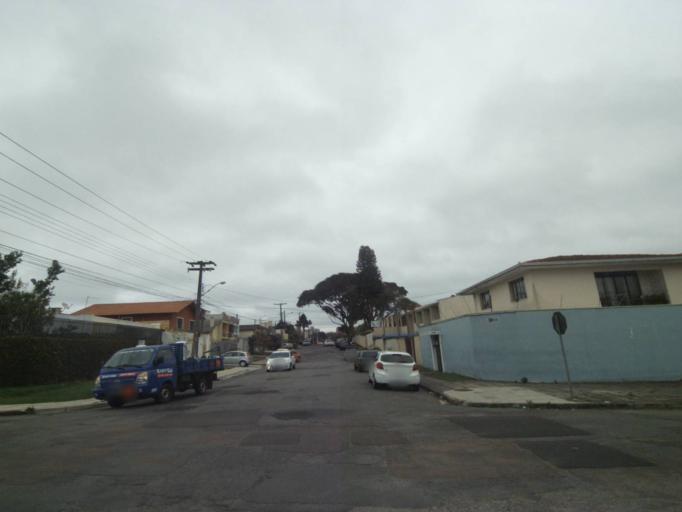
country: BR
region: Parana
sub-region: Curitiba
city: Curitiba
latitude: -25.4716
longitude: -49.2800
